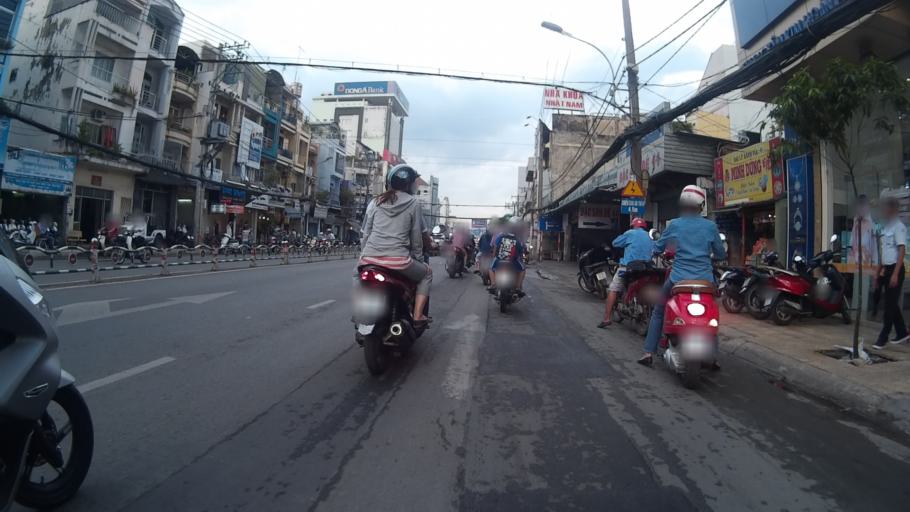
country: VN
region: Ho Chi Minh City
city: Quan Phu Nhuan
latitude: 10.8011
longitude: 106.6826
